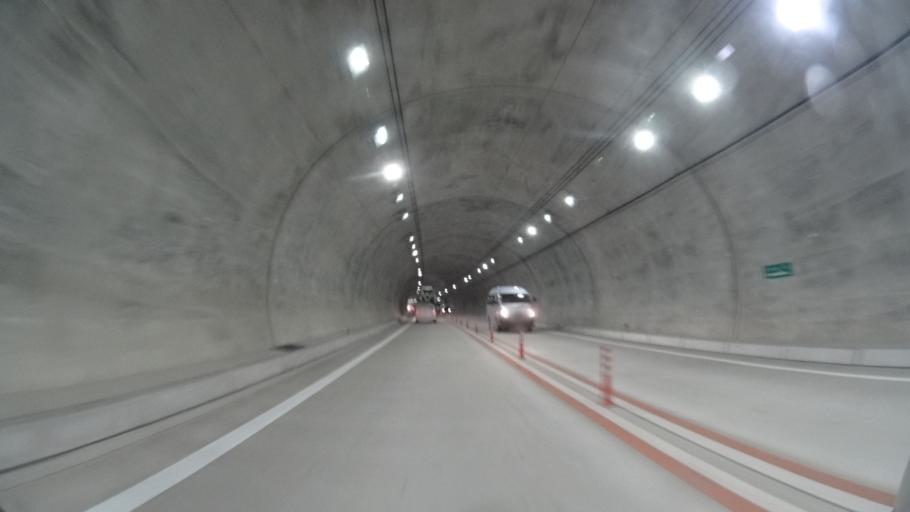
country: JP
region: Tottori
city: Tottori
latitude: 35.4961
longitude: 134.1718
